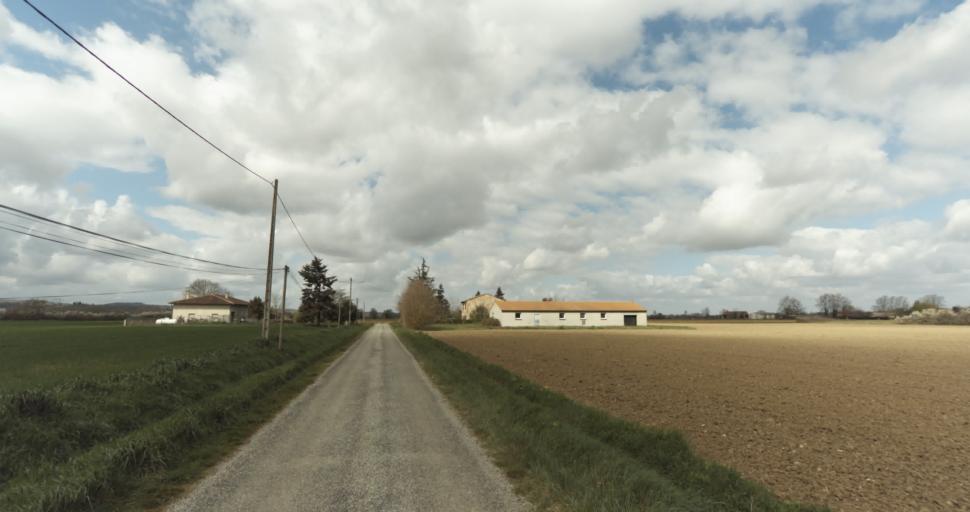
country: FR
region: Midi-Pyrenees
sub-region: Departement de la Haute-Garonne
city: Auterive
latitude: 43.3267
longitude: 1.4689
